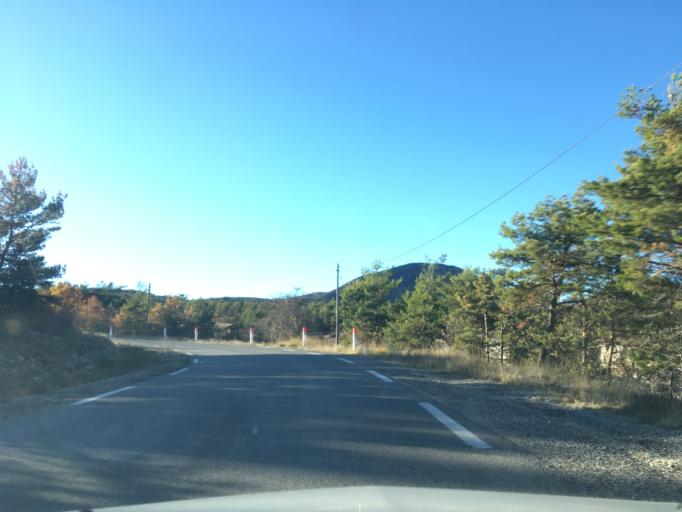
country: FR
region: Provence-Alpes-Cote d'Azur
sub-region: Departement des Alpes-de-Haute-Provence
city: Castellane
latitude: 43.7508
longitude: 6.4363
